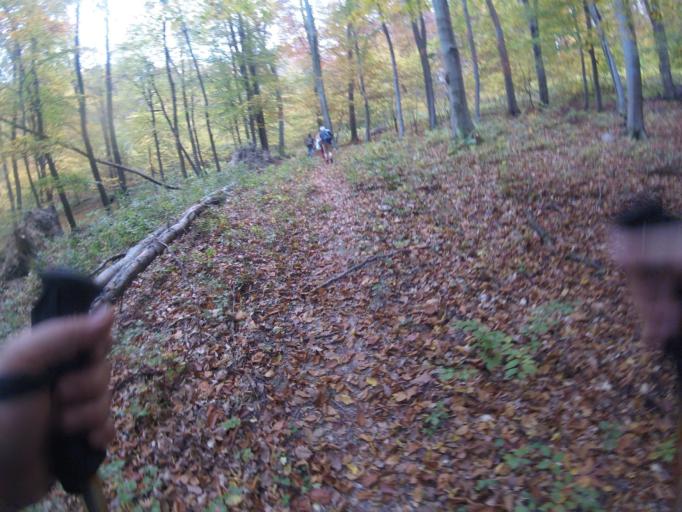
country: HU
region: Borsod-Abauj-Zemplen
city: Gonc
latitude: 48.4611
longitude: 21.3122
